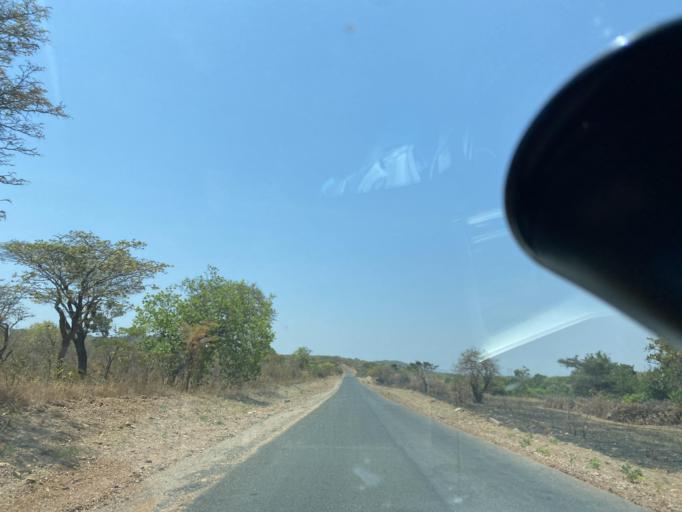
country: ZM
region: Lusaka
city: Kafue
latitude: -15.8381
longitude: 28.4059
